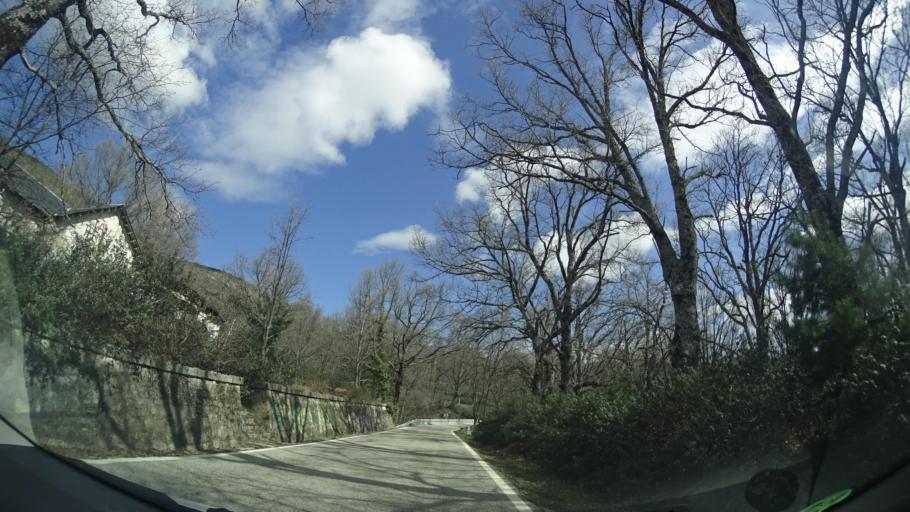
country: ES
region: Madrid
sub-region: Provincia de Madrid
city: Miraflores de la Sierra
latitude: 40.8426
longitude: -3.7663
